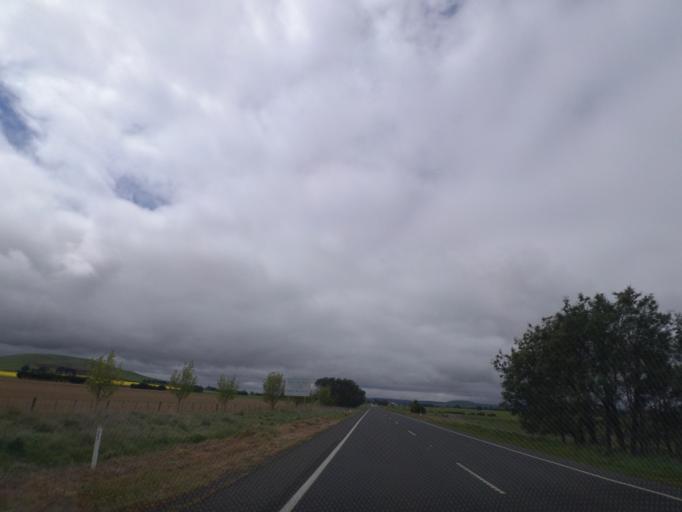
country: AU
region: Victoria
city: Brown Hill
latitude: -37.4098
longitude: 143.9469
